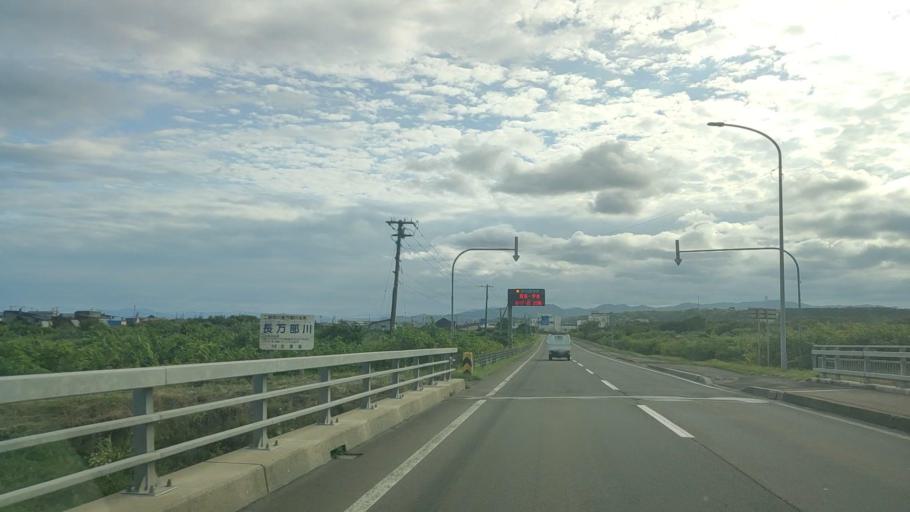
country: JP
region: Hokkaido
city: Niseko Town
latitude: 42.5235
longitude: 140.3874
